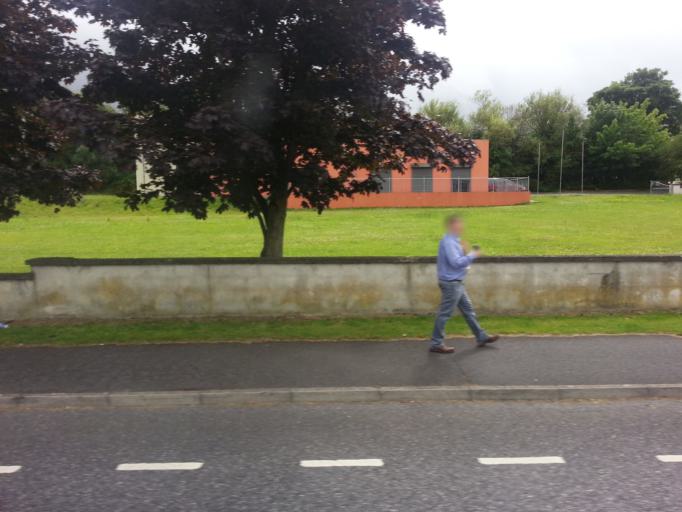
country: IE
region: Leinster
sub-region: Kilkenny
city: Kilkenny
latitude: 52.6442
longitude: -7.2374
